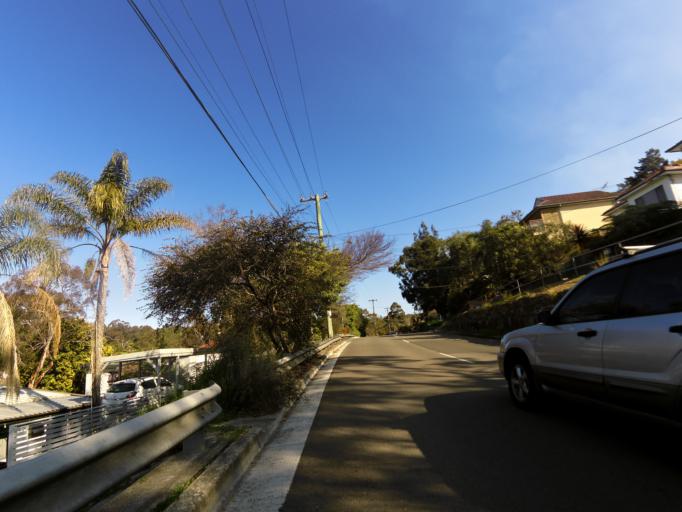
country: AU
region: New South Wales
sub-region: Sutherland Shire
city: Oyster Bay
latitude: -34.0081
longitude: 151.0693
